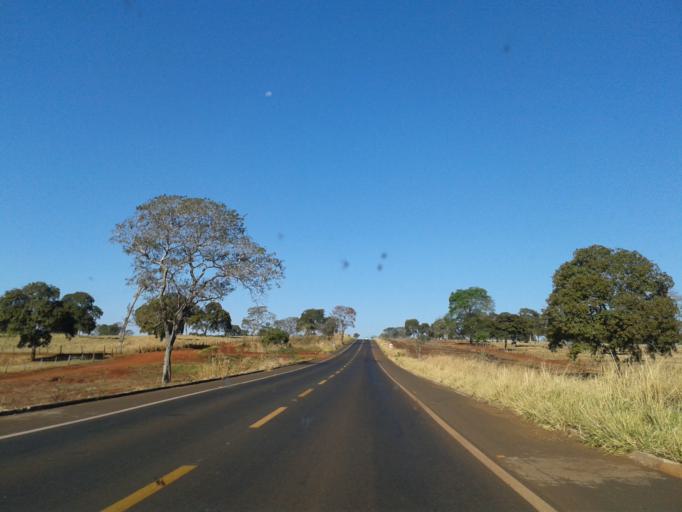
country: BR
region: Minas Gerais
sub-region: Santa Vitoria
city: Santa Vitoria
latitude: -18.9333
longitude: -49.8329
